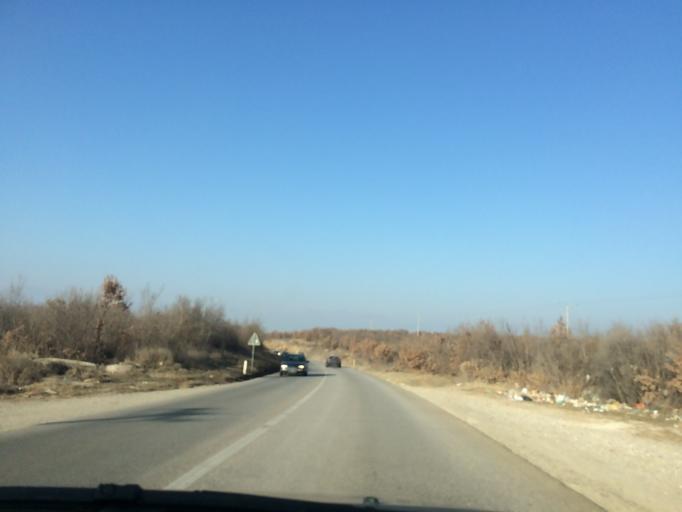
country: XK
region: Pec
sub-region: Komuna e Klines
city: Klina
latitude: 42.5969
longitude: 20.6263
